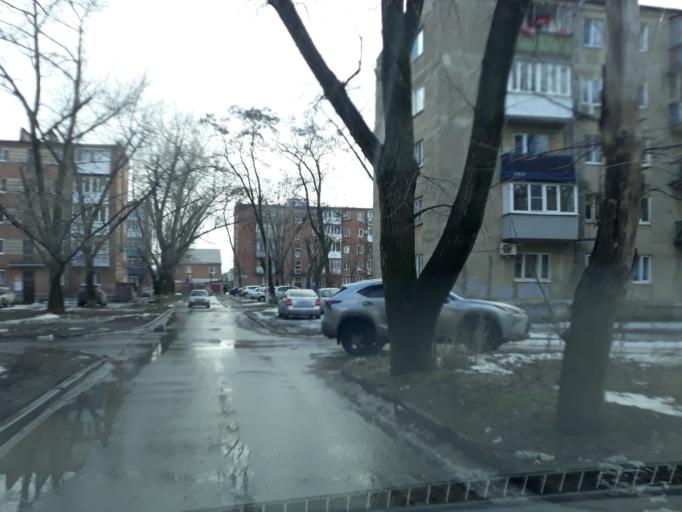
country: RU
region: Rostov
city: Taganrog
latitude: 47.2512
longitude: 38.9130
